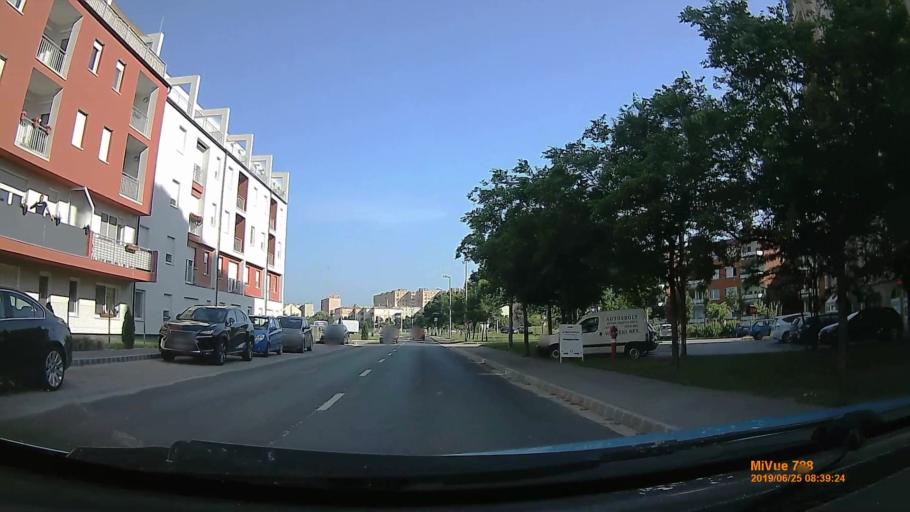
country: HU
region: Fejer
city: Szekesfehervar
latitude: 47.1849
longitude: 18.4021
